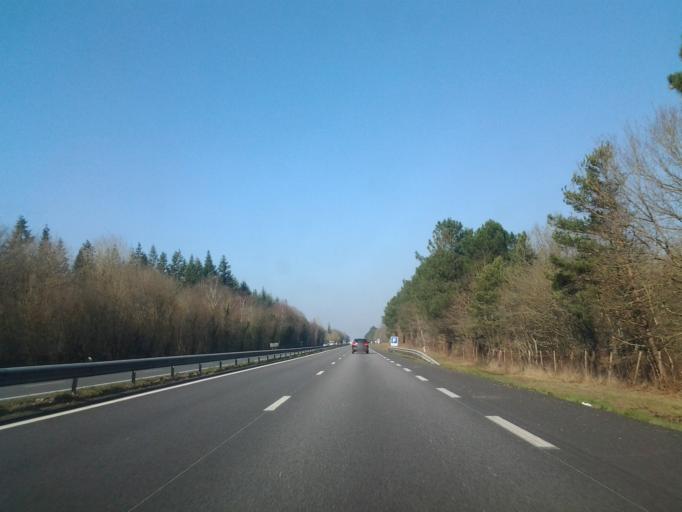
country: FR
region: Pays de la Loire
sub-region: Departement de la Vendee
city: Aizenay
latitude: 46.7274
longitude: -1.5725
